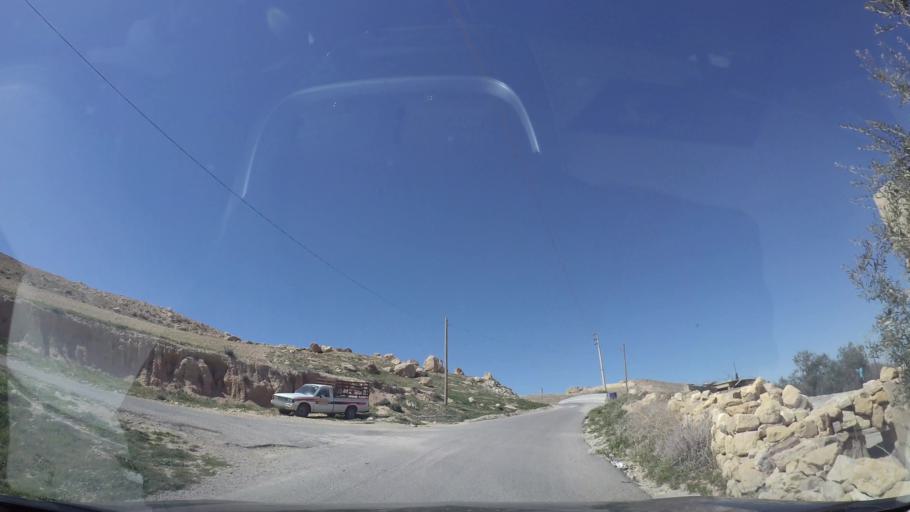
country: JO
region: Tafielah
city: At Tafilah
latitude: 30.8403
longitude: 35.5654
